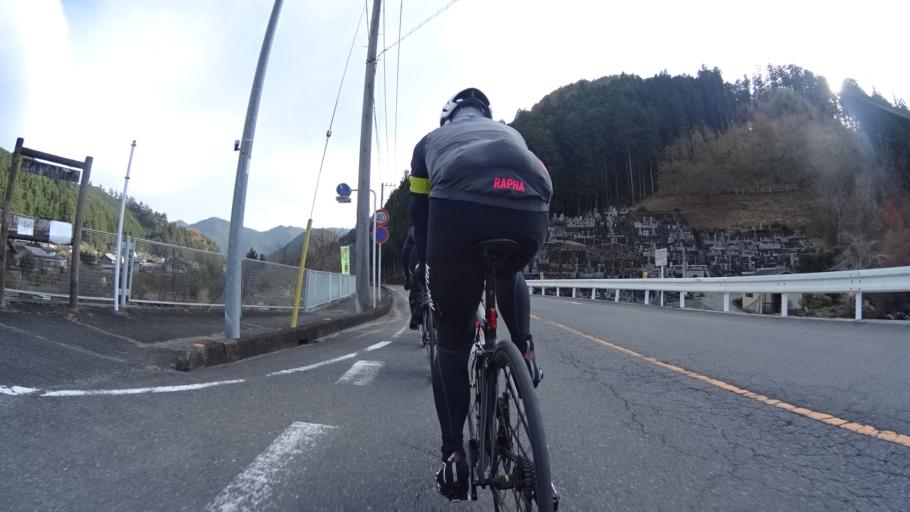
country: JP
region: Tokyo
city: Ome
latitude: 35.8605
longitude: 139.1881
